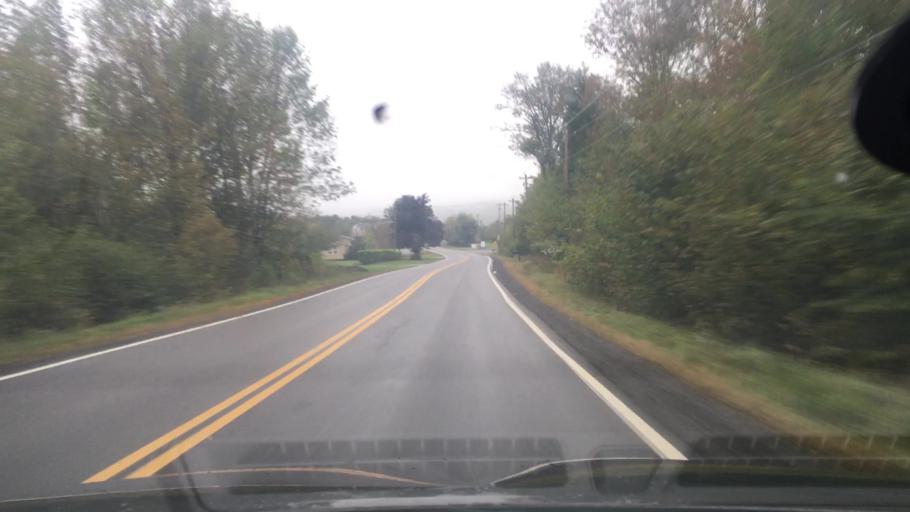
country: CA
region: Nova Scotia
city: Windsor
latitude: 44.9430
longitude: -64.1848
